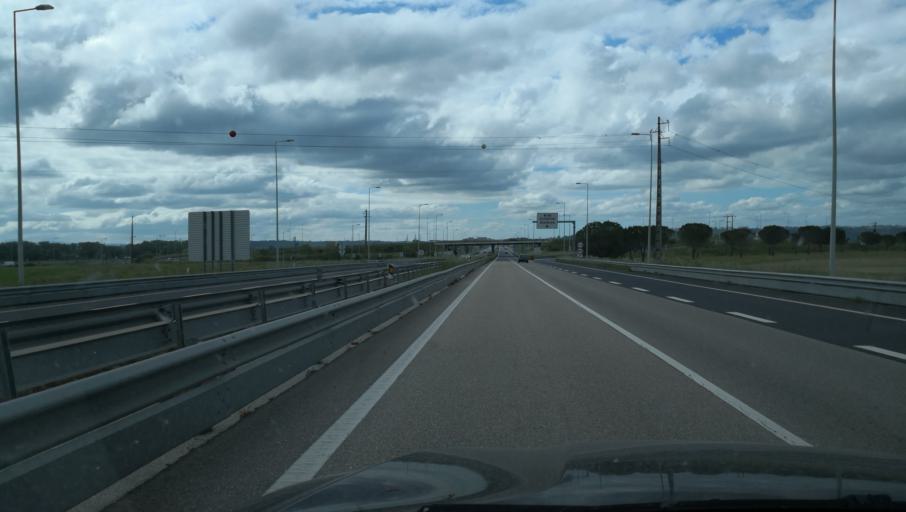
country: PT
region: Santarem
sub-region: Almeirim
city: Almeirim
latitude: 39.1883
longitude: -8.6450
